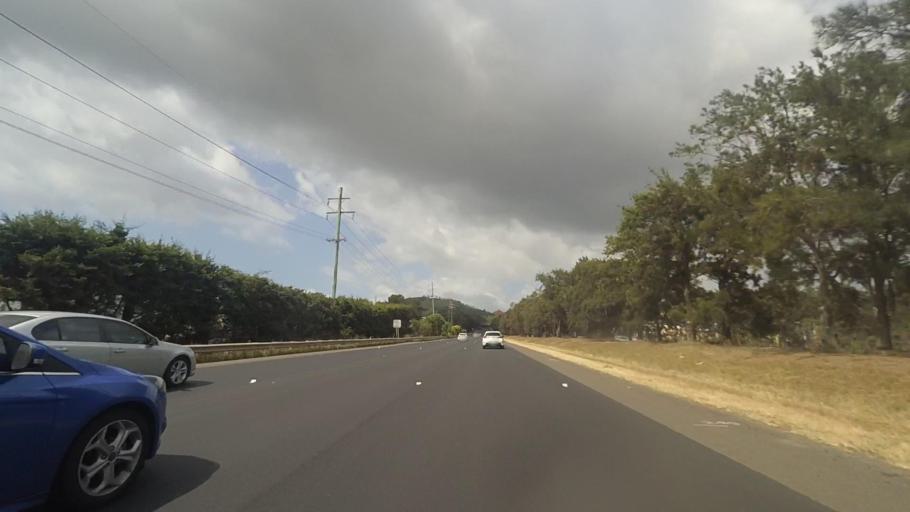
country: AU
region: New South Wales
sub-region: Wollongong
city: Mount Saint Thomas
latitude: -34.4582
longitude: 150.8553
